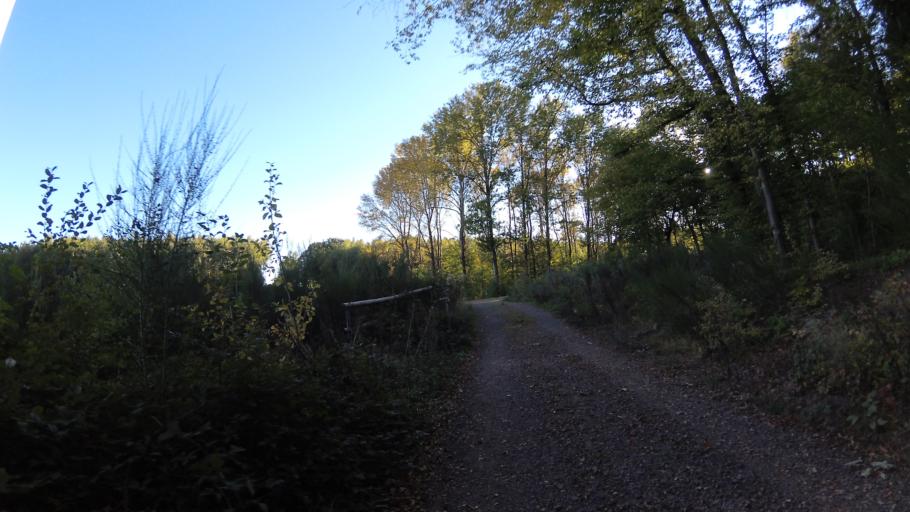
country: DE
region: Saarland
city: Ottweiler
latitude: 49.4291
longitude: 7.1936
